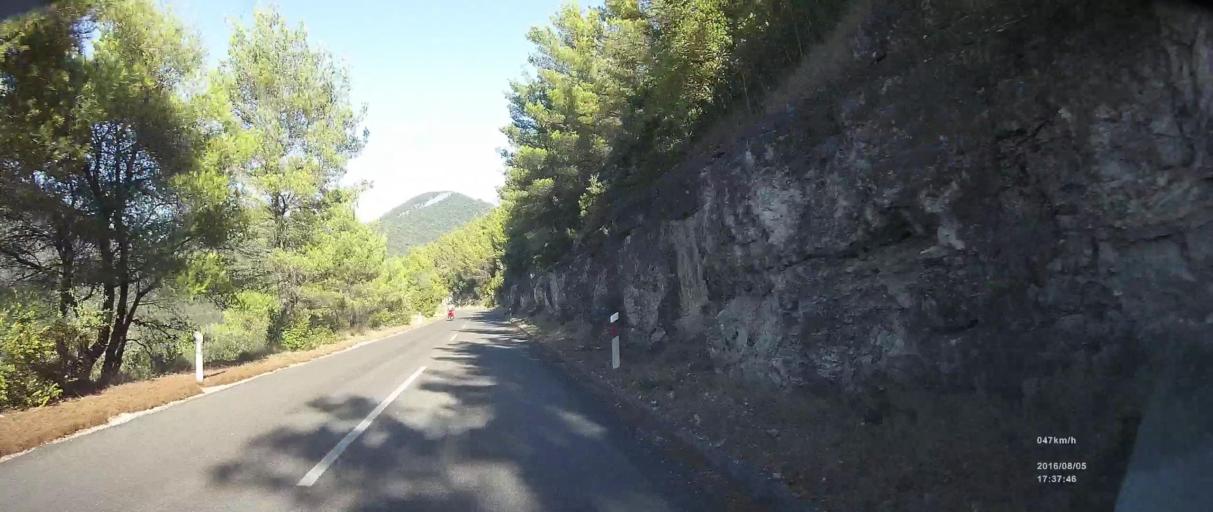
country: HR
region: Dubrovacko-Neretvanska
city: Blato
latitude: 42.7570
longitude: 17.4732
